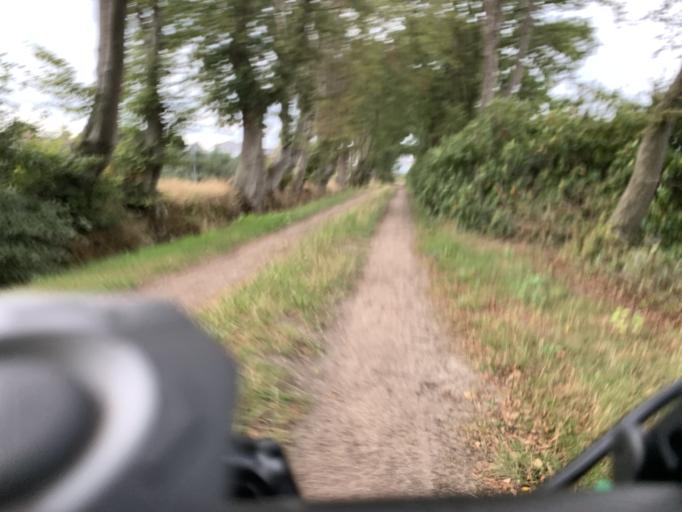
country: DE
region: Lower Saxony
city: Westerstede
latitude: 53.2458
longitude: 7.9097
